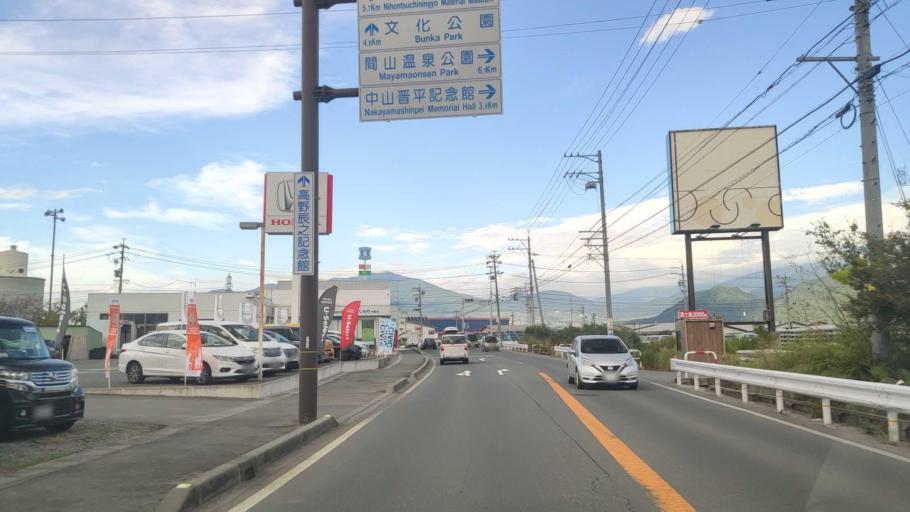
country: JP
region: Nagano
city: Nakano
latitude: 36.7299
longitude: 138.3413
